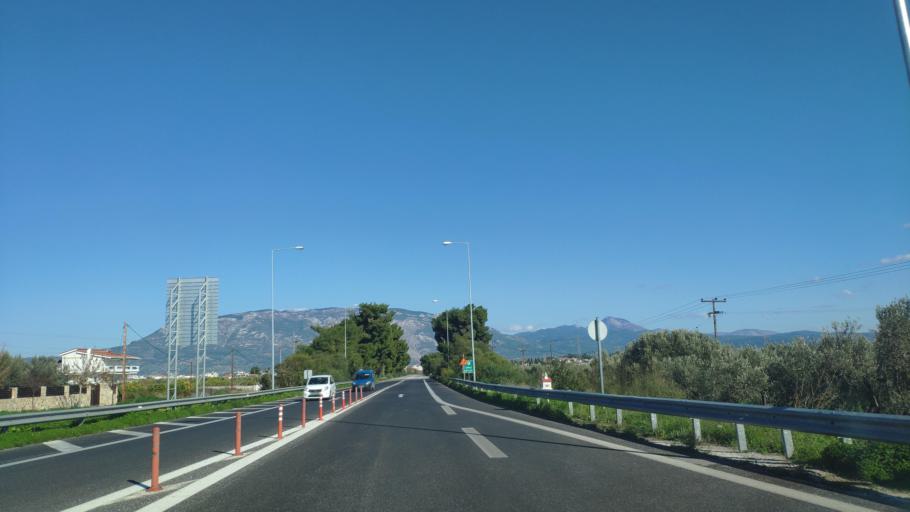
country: GR
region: Peloponnese
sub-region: Nomos Korinthias
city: Examilia
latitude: 37.9219
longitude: 22.9116
